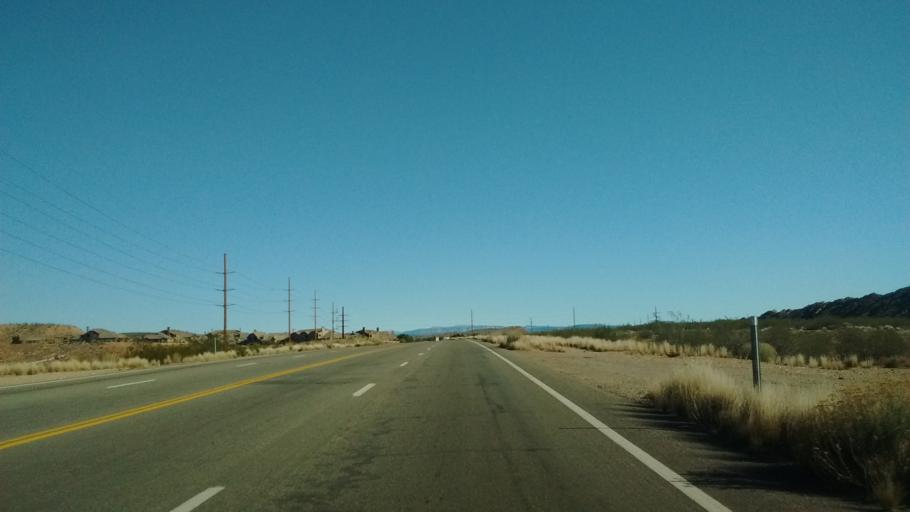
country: US
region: Utah
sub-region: Washington County
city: Washington
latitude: 37.1527
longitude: -113.4453
